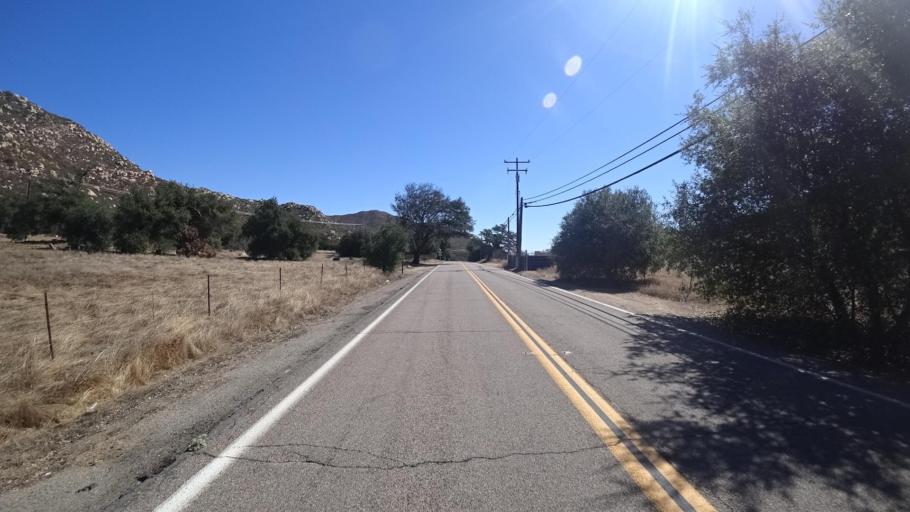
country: US
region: California
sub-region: San Diego County
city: Alpine
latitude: 32.7119
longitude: -116.7462
